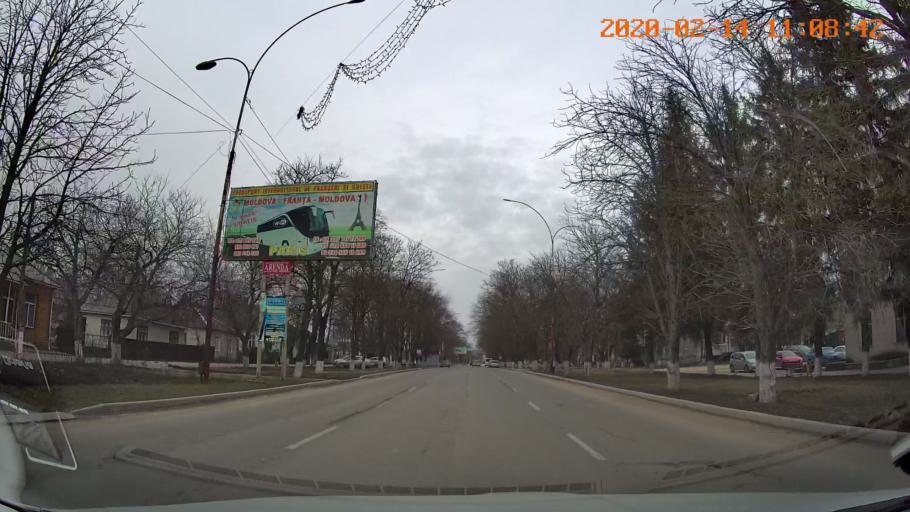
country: MD
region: Raionul Edinet
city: Edinet
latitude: 48.1735
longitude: 27.2999
